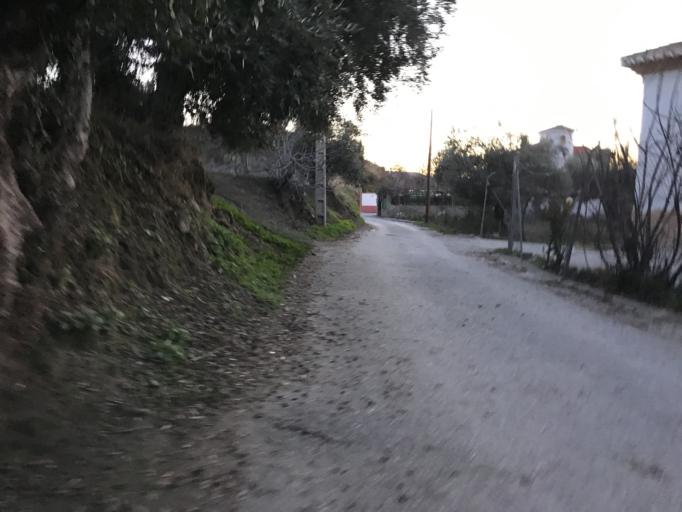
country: ES
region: Andalusia
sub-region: Provincia de Granada
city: Beas de Granada
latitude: 37.2228
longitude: -3.4787
